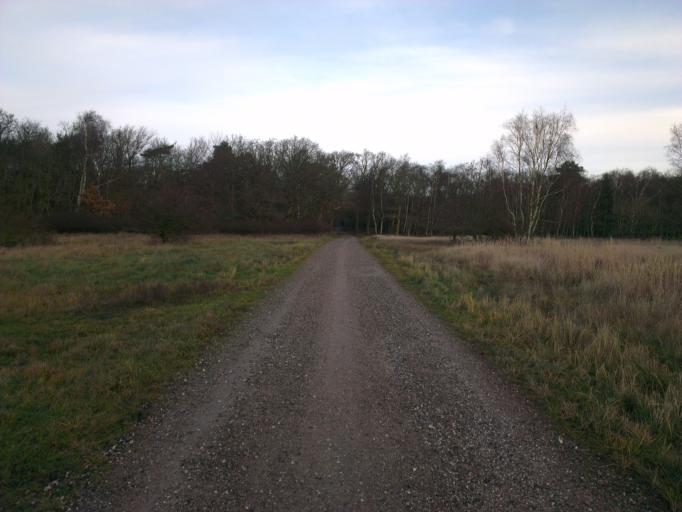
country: DK
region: Capital Region
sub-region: Frederikssund Kommune
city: Jaegerspris
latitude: 55.8446
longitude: 11.9631
